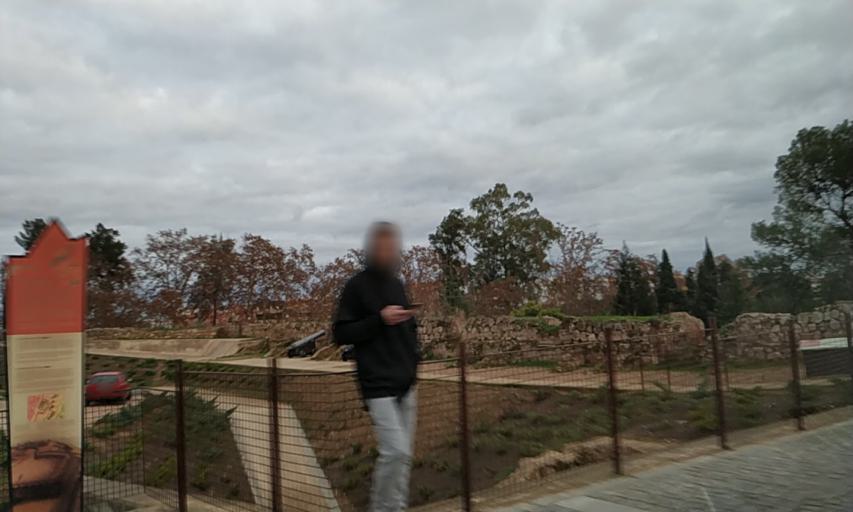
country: ES
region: Extremadura
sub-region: Provincia de Badajoz
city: Badajoz
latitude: 38.8799
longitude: -6.9655
